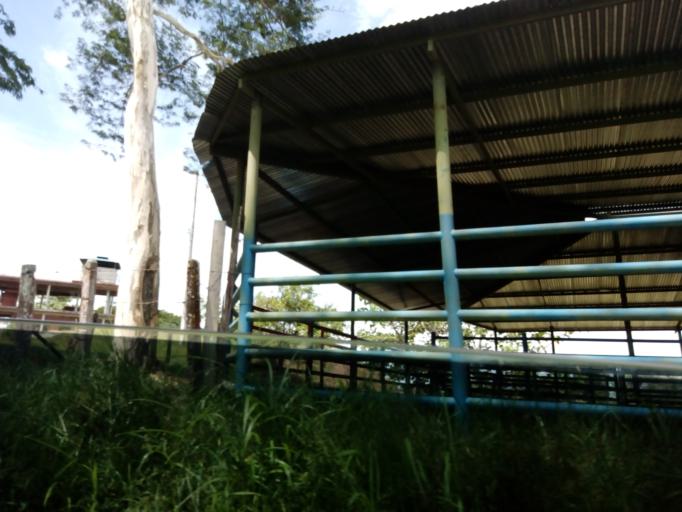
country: CO
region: Boyaca
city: Puerto Boyaca
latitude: 5.9655
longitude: -74.4437
